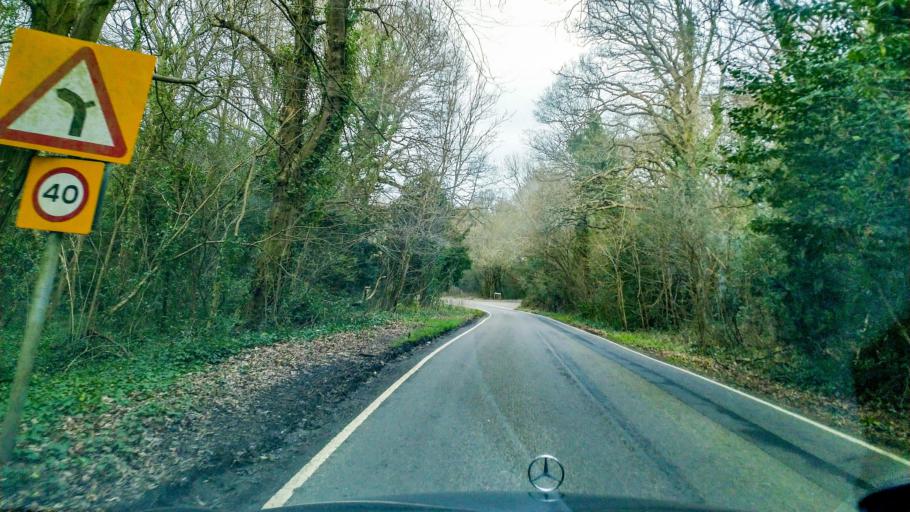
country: GB
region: England
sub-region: Surrey
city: Dorking
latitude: 51.2110
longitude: -0.3264
